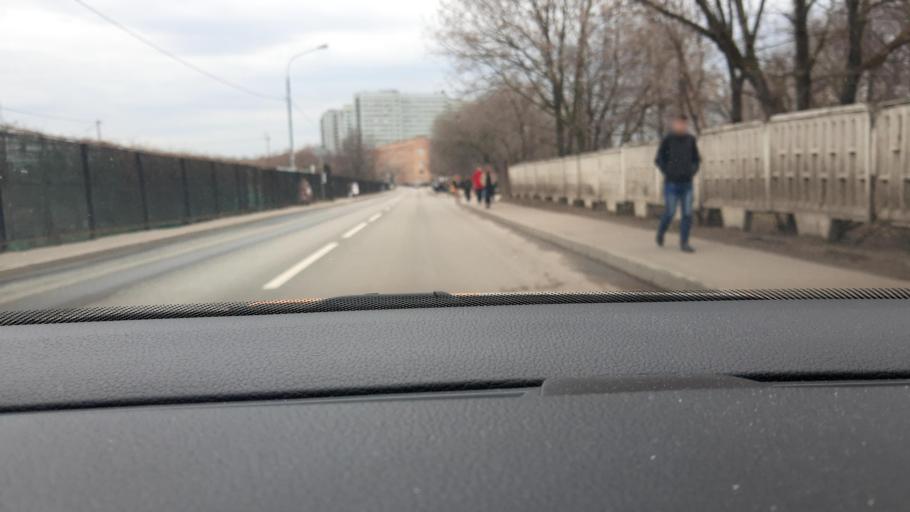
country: RU
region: Moscow
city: Likhobory
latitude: 55.8344
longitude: 37.5614
